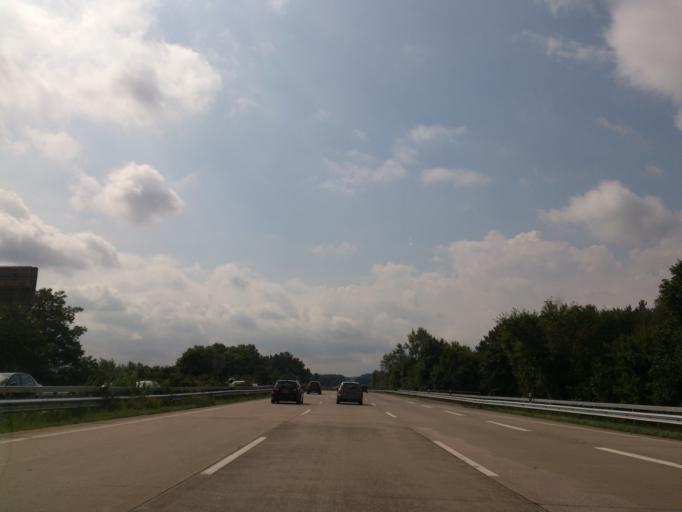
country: DE
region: Lower Saxony
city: Brackel
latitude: 53.3036
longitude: 10.0729
